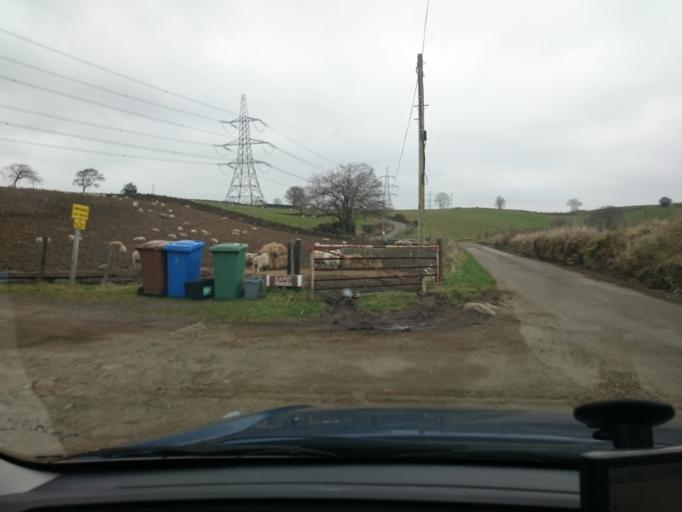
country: GB
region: Scotland
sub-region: Falkirk
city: Dunipace
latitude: 56.0010
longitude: -3.9443
